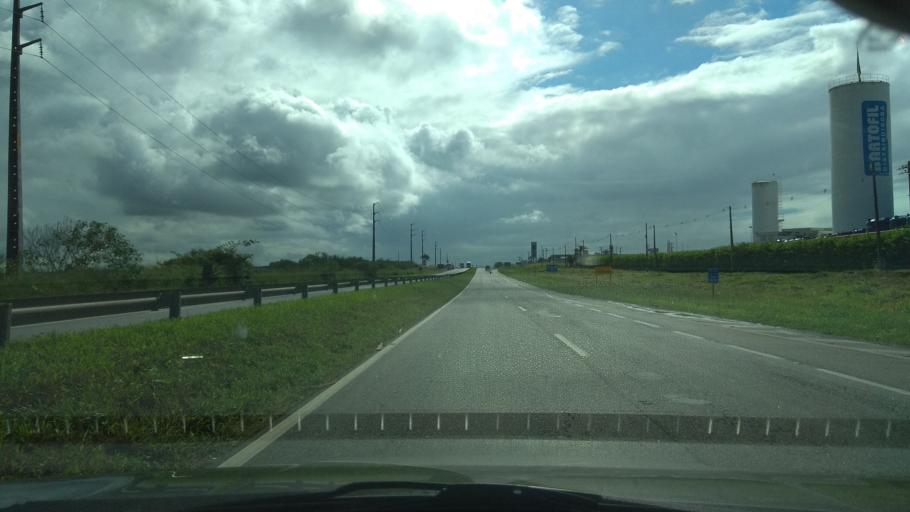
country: BR
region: Bahia
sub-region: Conceicao Do Jacuipe
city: Conceicao do Jacuipe
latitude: -12.3428
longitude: -38.8422
